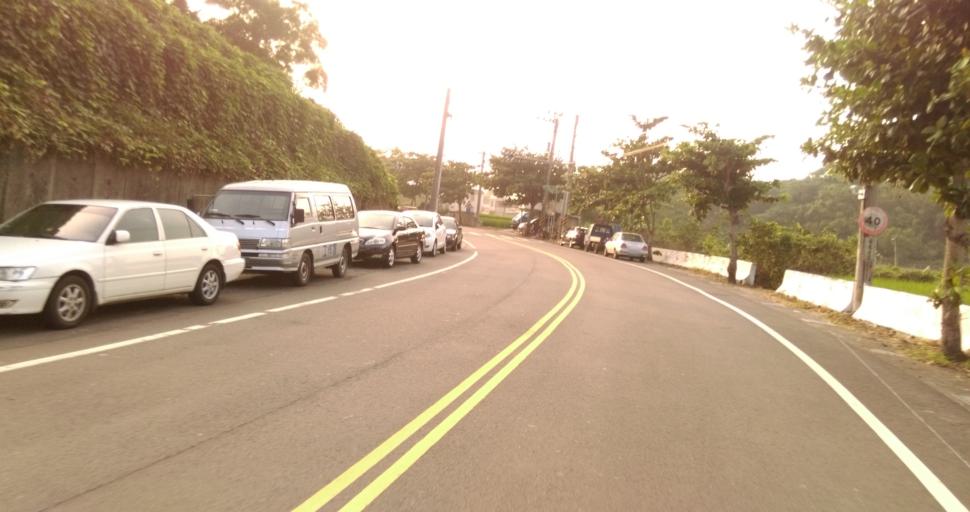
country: TW
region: Taiwan
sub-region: Hsinchu
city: Hsinchu
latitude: 24.7462
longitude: 120.9347
